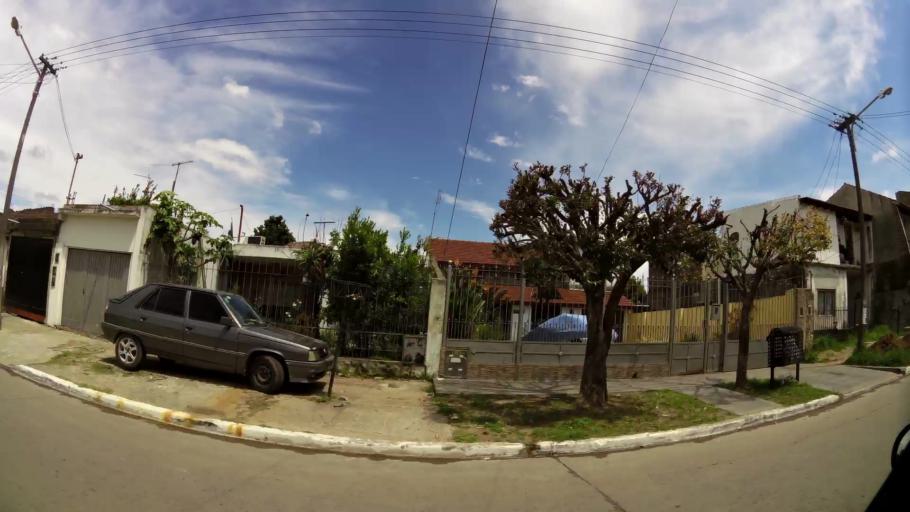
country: AR
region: Buenos Aires
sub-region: Partido de Quilmes
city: Quilmes
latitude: -34.7869
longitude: -58.2661
